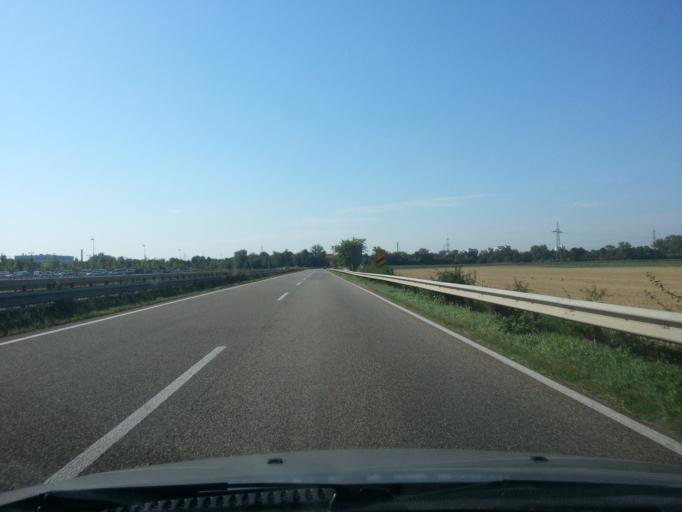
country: DE
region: Rheinland-Pfalz
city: Frankenthal
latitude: 49.5547
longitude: 8.3967
